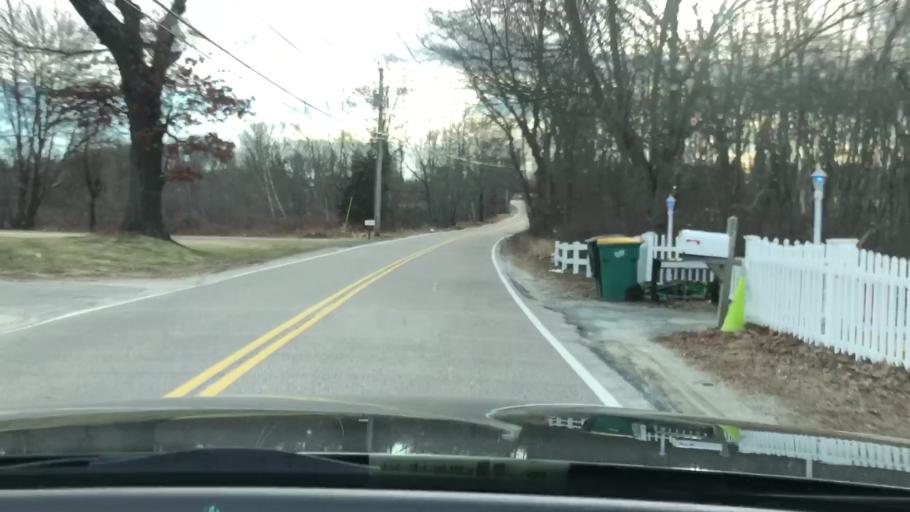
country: US
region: Massachusetts
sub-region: Worcester County
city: Blackstone
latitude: 42.0578
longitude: -71.5289
